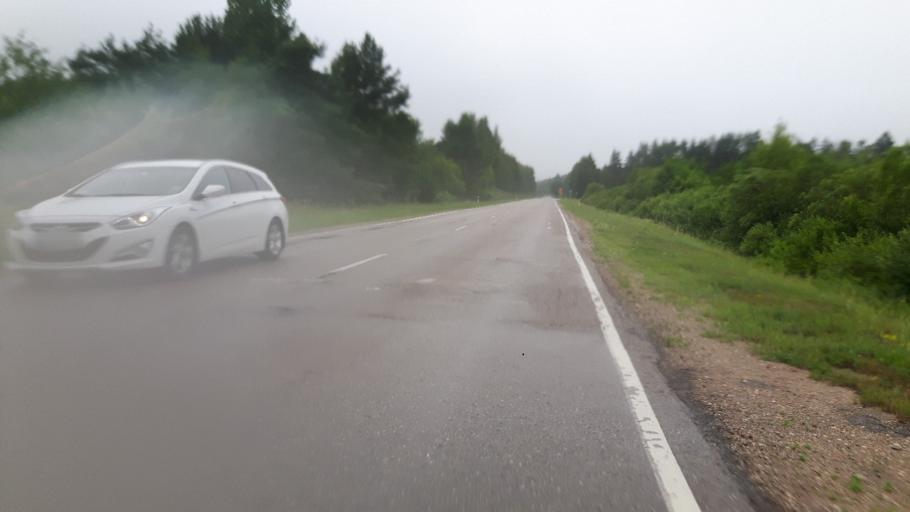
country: LV
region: Rucavas
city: Rucava
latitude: 56.1036
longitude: 21.1355
